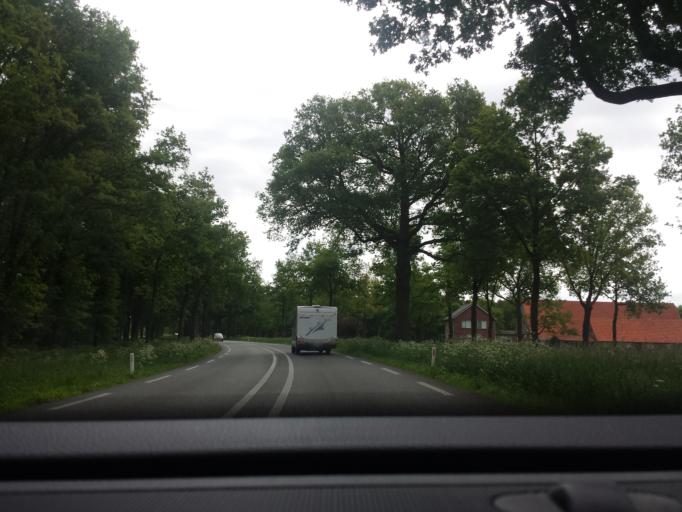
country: NL
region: Gelderland
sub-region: Oost Gelre
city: Lichtenvoorde
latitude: 52.0397
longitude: 6.5720
